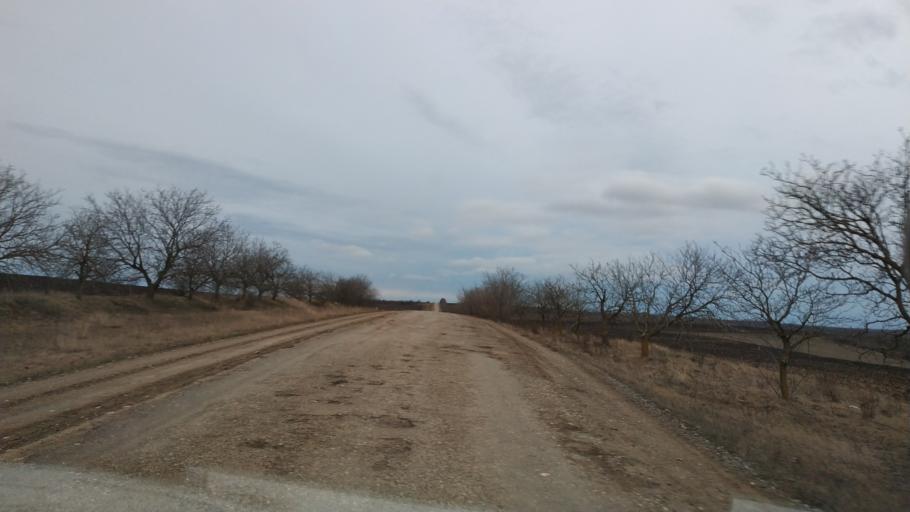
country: MD
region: Causeni
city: Causeni
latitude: 46.5744
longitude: 29.3892
